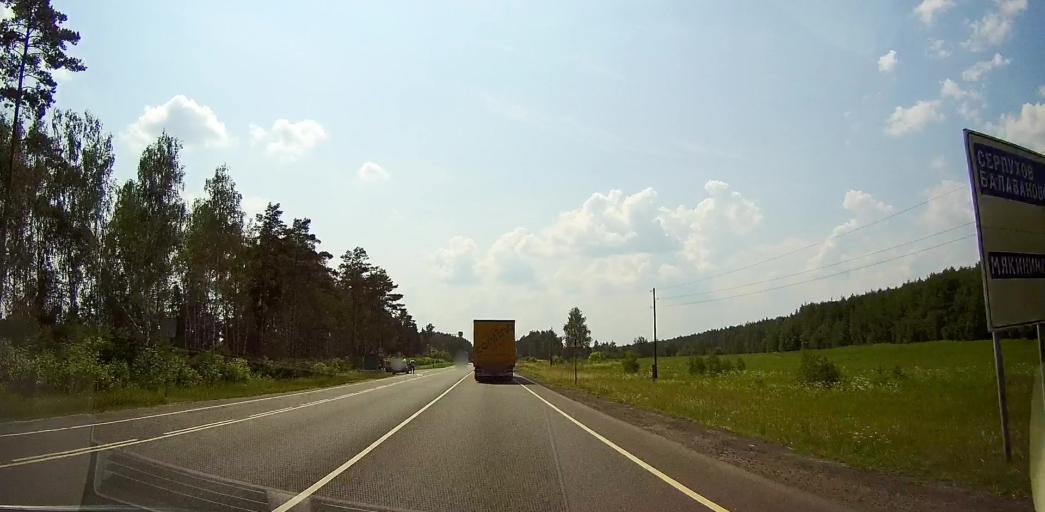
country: RU
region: Moskovskaya
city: Meshcherino
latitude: 55.1752
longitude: 38.3347
